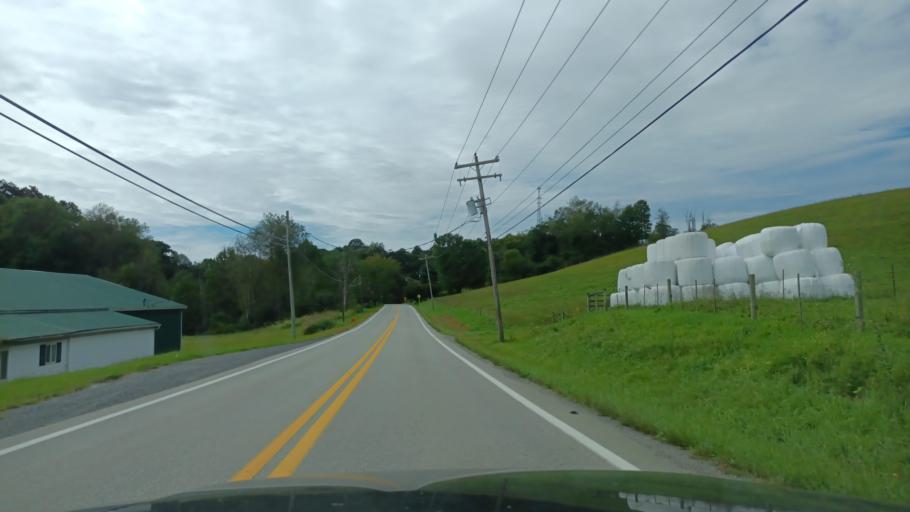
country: US
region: West Virginia
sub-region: Taylor County
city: Grafton
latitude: 39.3295
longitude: -80.0966
